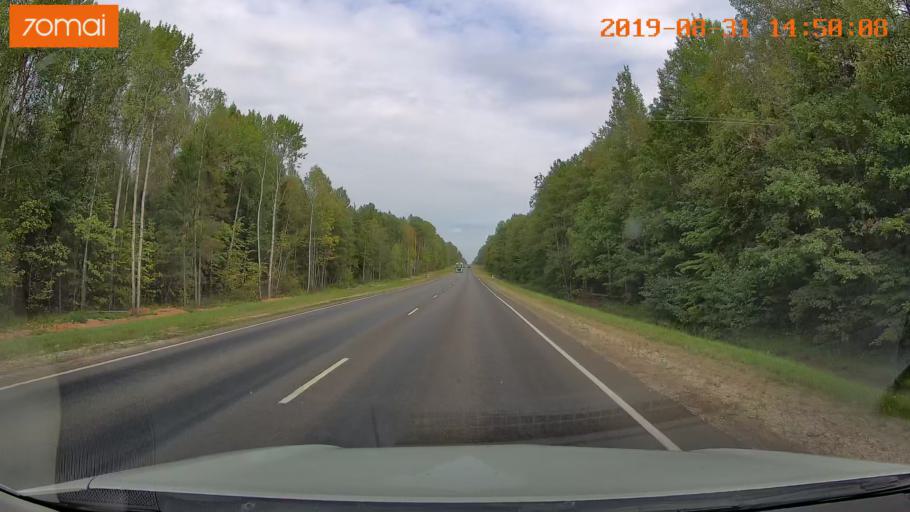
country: RU
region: Kaluga
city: Spas-Demensk
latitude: 54.2592
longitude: 33.7824
